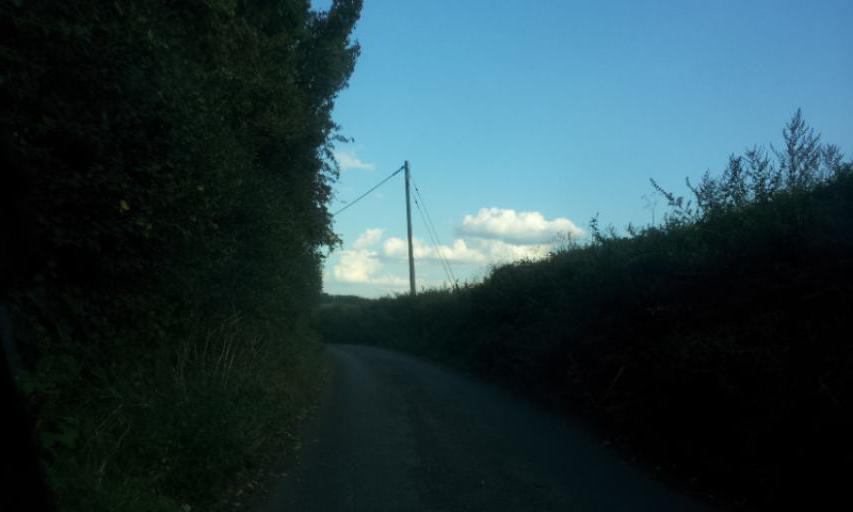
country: GB
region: England
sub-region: Kent
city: Longfield
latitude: 51.4058
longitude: 0.2605
